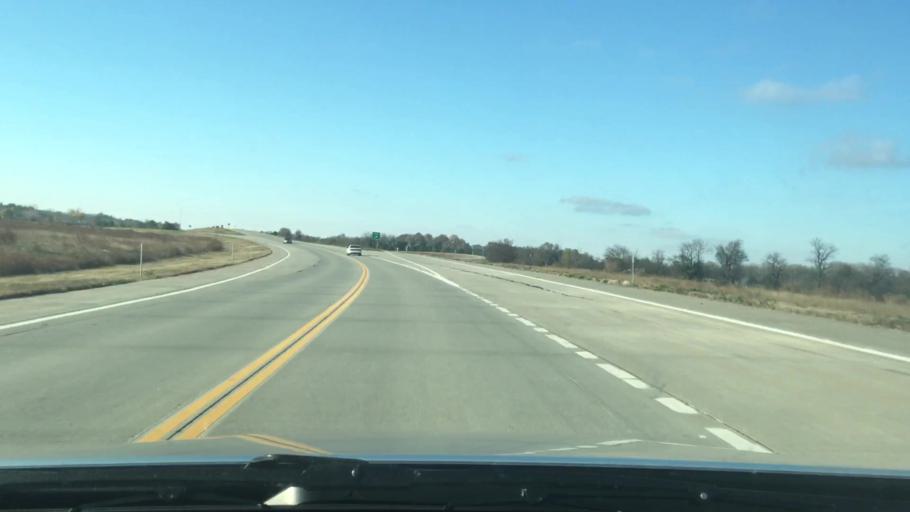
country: US
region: Kansas
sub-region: Reno County
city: Hutchinson
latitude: 38.0874
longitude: -97.9915
